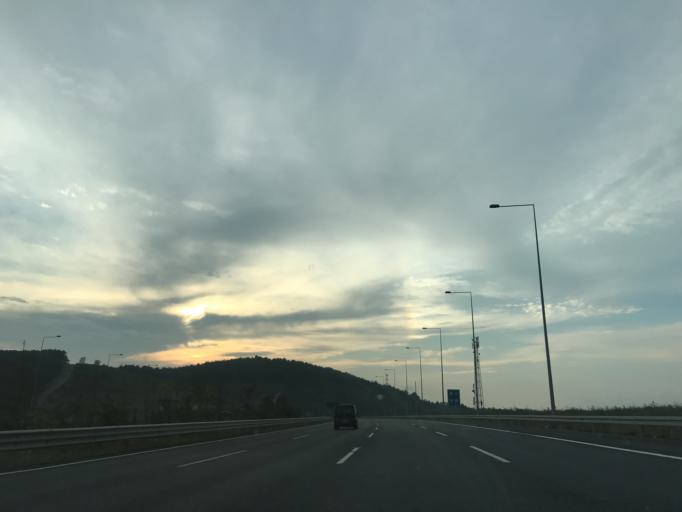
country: TR
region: Istanbul
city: Samandira
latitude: 41.0554
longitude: 29.1876
